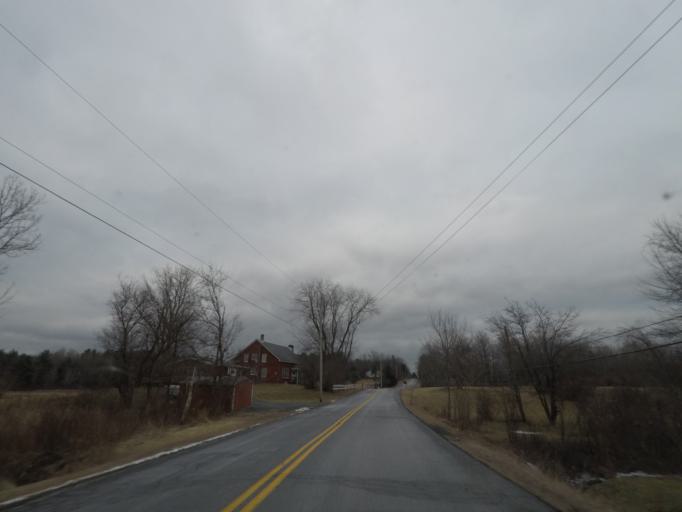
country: US
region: New York
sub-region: Rensselaer County
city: Poestenkill
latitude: 42.7664
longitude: -73.4809
